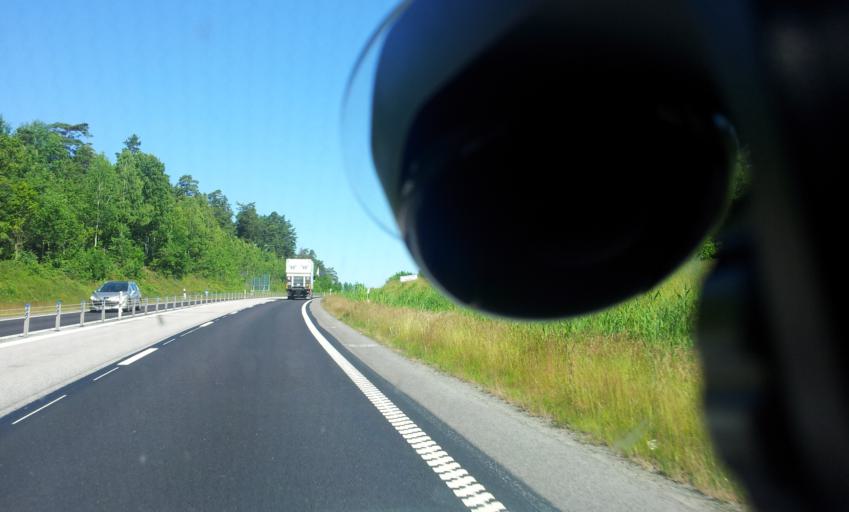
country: SE
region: OEstergoetland
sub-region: Soderkopings Kommun
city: Soederkoeping
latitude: 58.4944
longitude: 16.3048
